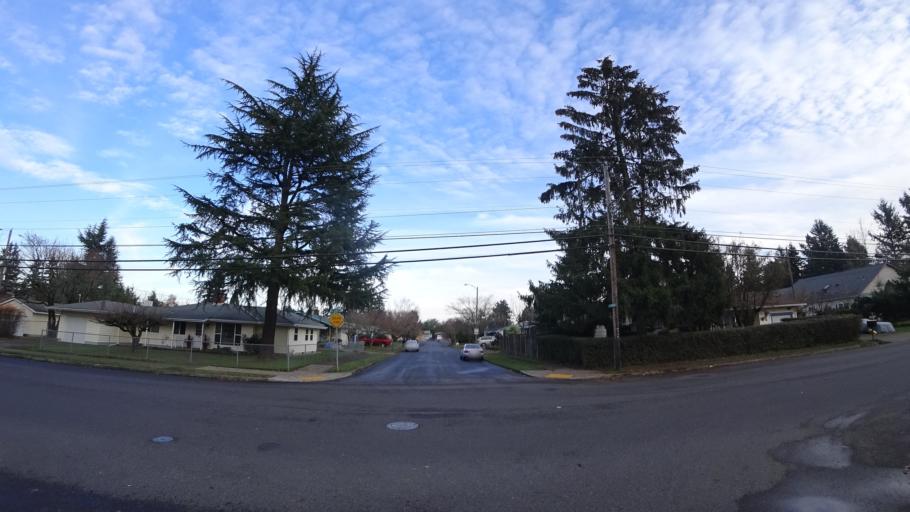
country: US
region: Oregon
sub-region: Multnomah County
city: Lents
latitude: 45.5166
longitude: -122.5301
